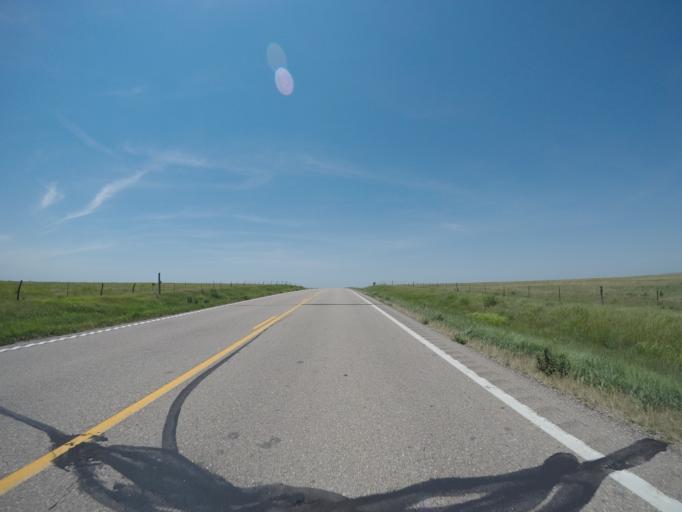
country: US
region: Kansas
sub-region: Dickinson County
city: Solomon
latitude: 39.0308
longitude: -97.4212
